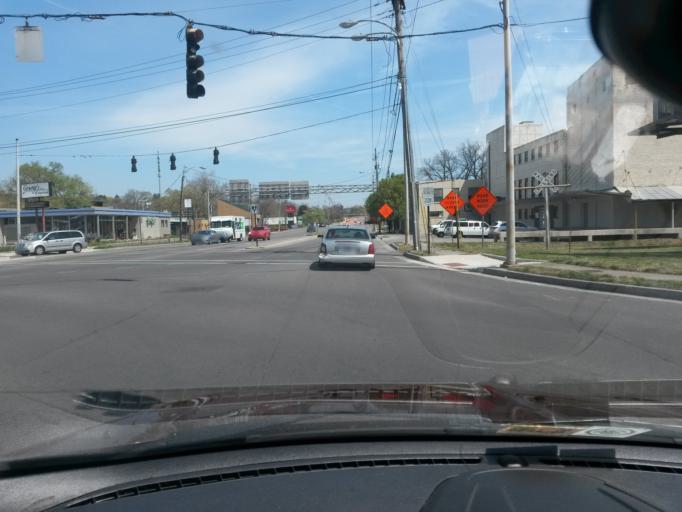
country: US
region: Virginia
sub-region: City of Roanoke
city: Cedar Bluff
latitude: 37.2532
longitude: -79.9515
